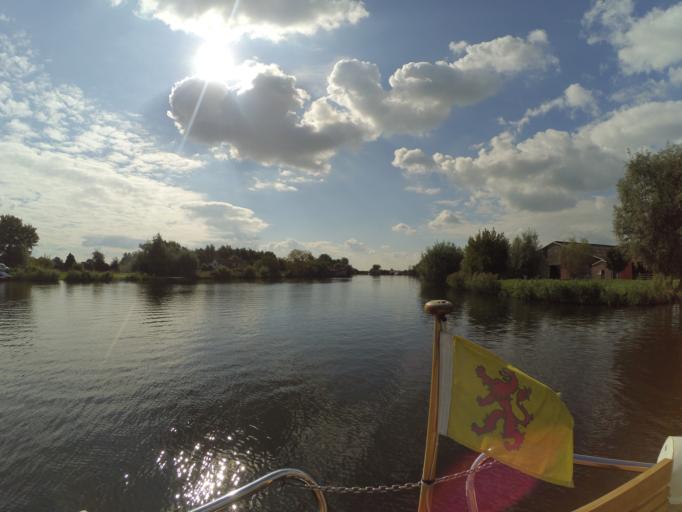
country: NL
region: Utrecht
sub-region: Stichtse Vecht
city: Vreeland
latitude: 52.2589
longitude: 5.0321
